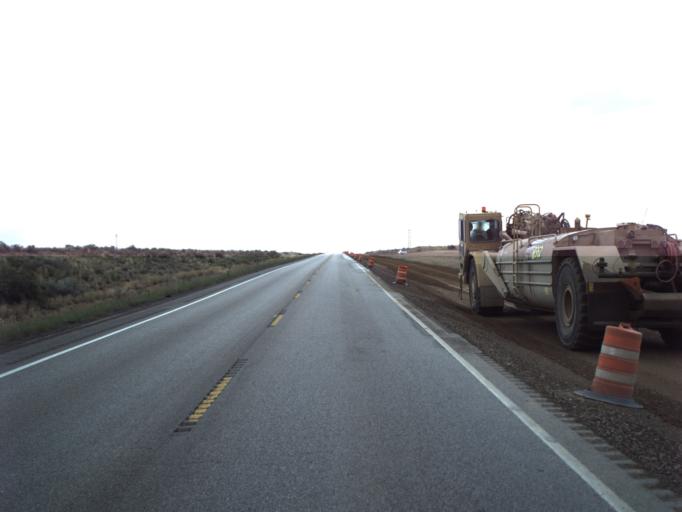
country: US
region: Utah
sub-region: Carbon County
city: East Carbon City
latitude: 39.4506
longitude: -110.4753
